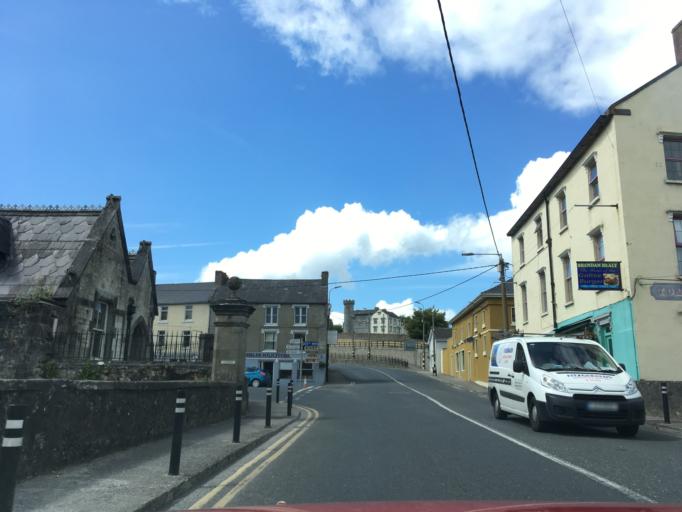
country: IE
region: Munster
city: Cahir
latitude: 52.3758
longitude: -7.9286
